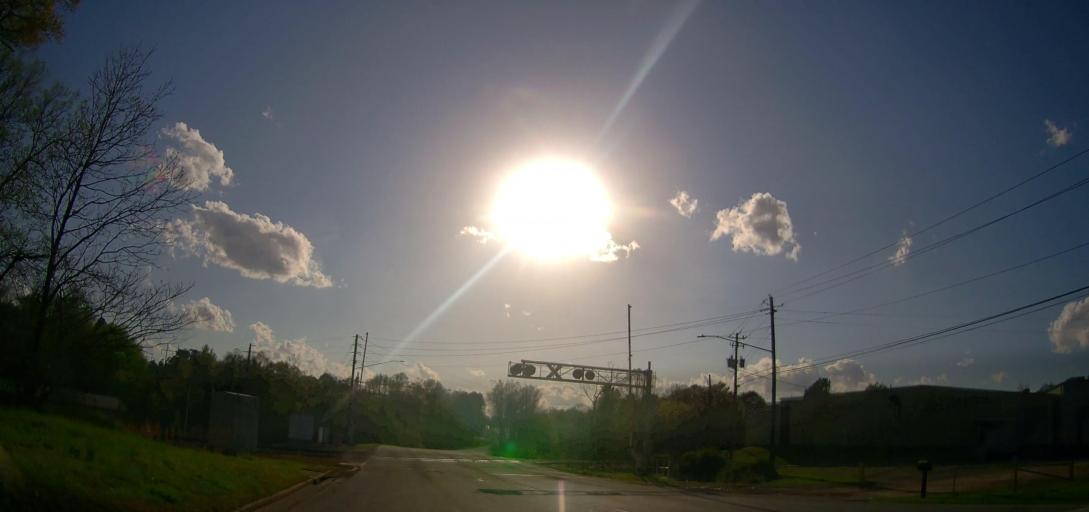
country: US
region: Georgia
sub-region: Baldwin County
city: Milledgeville
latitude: 33.0919
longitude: -83.2400
